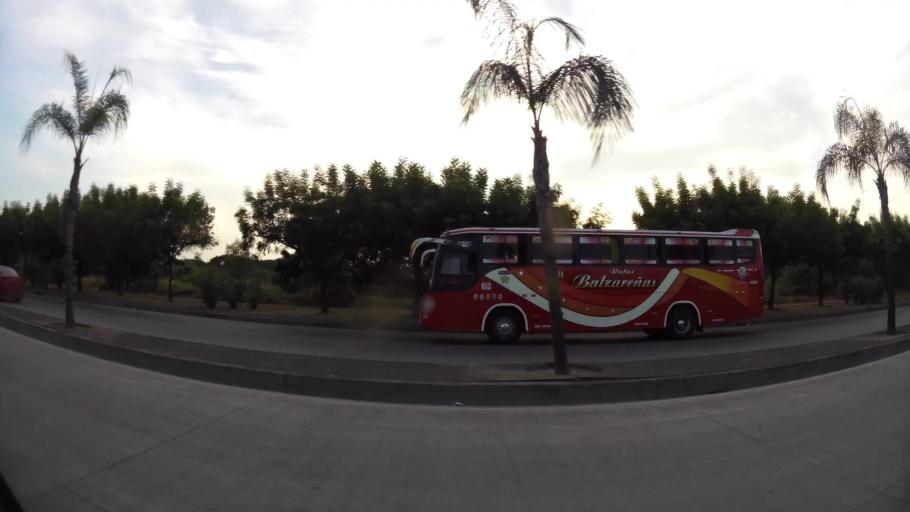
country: EC
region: Guayas
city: Eloy Alfaro
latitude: -2.0972
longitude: -79.8917
